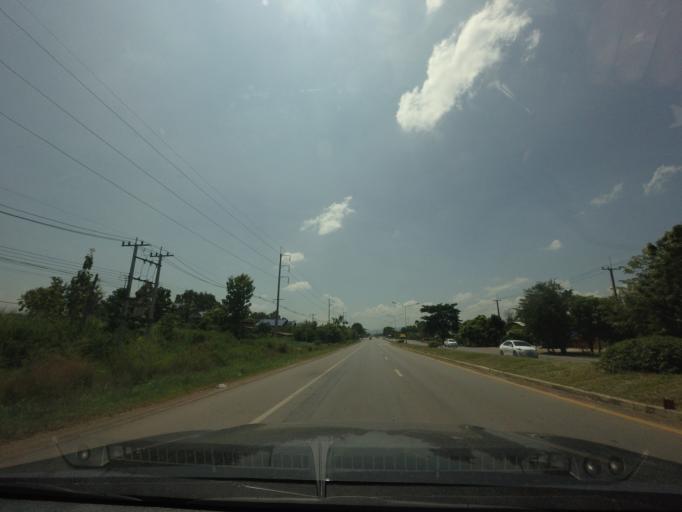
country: TH
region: Phetchabun
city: Lom Sak
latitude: 16.7228
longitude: 101.1848
